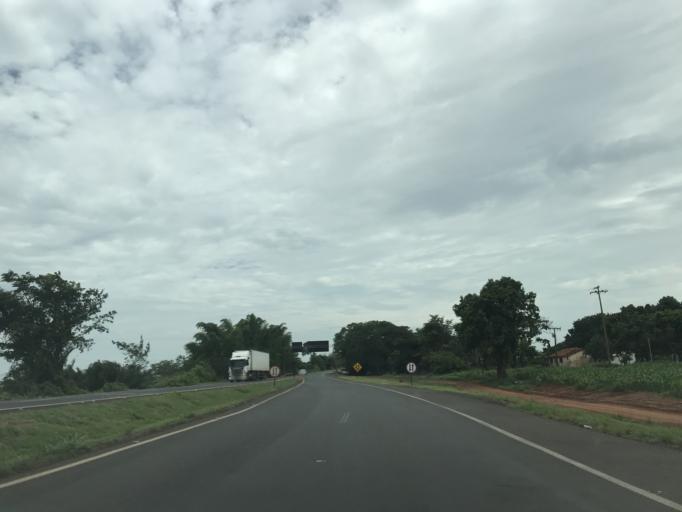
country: BR
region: Minas Gerais
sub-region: Frutal
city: Frutal
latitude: -20.1390
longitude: -49.1101
